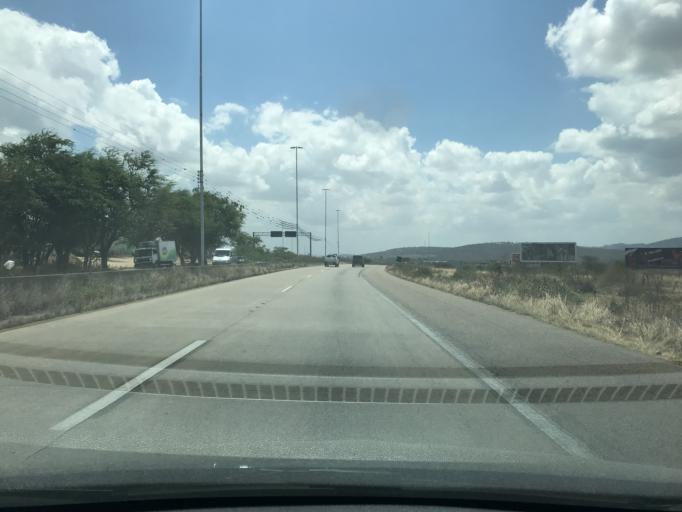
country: BR
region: Pernambuco
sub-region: Bezerros
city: Bezerros
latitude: -8.2998
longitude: -35.8518
